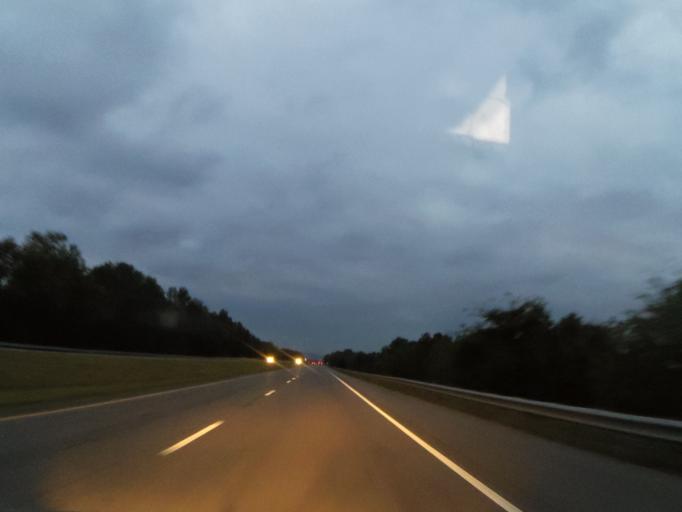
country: US
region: Alabama
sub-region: Madison County
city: New Hope
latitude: 34.6267
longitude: -86.3110
